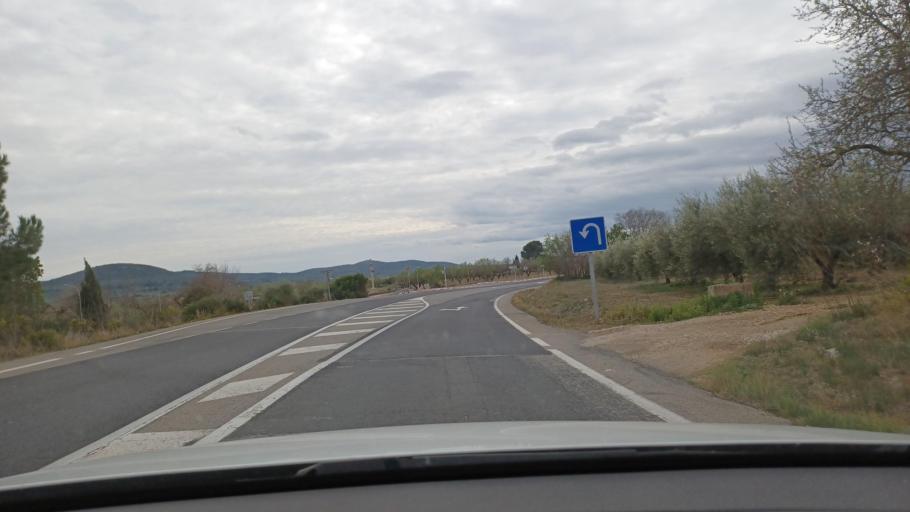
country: ES
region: Catalonia
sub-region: Provincia de Tarragona
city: Santa Barbara
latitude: 40.6791
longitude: 0.4584
